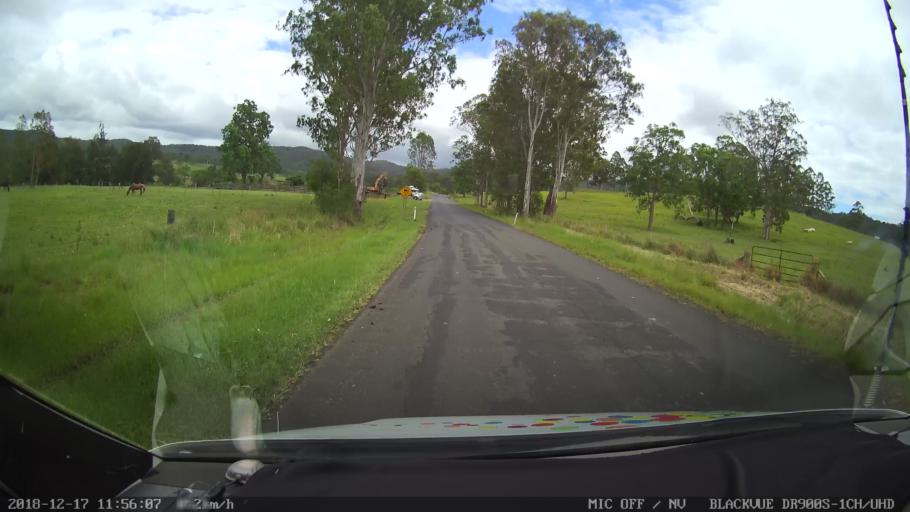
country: AU
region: New South Wales
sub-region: Kyogle
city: Kyogle
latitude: -28.5500
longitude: 152.5818
